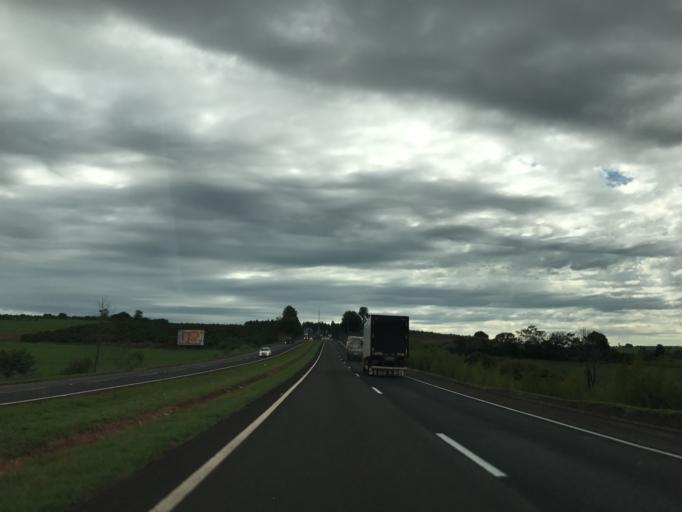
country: BR
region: Parana
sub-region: Rolandia
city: Rolandia
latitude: -23.3101
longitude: -51.3311
